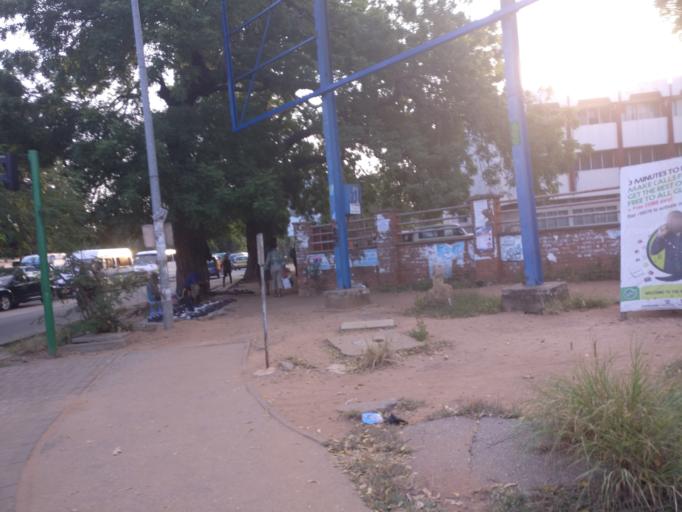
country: GH
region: Greater Accra
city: Accra
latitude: 5.5512
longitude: -0.1988
